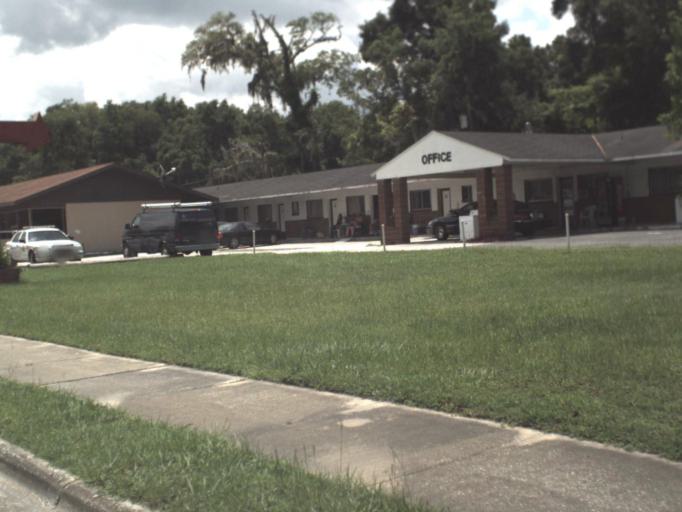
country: US
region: Florida
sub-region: Levy County
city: Bronson
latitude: 29.4471
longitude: -82.6414
